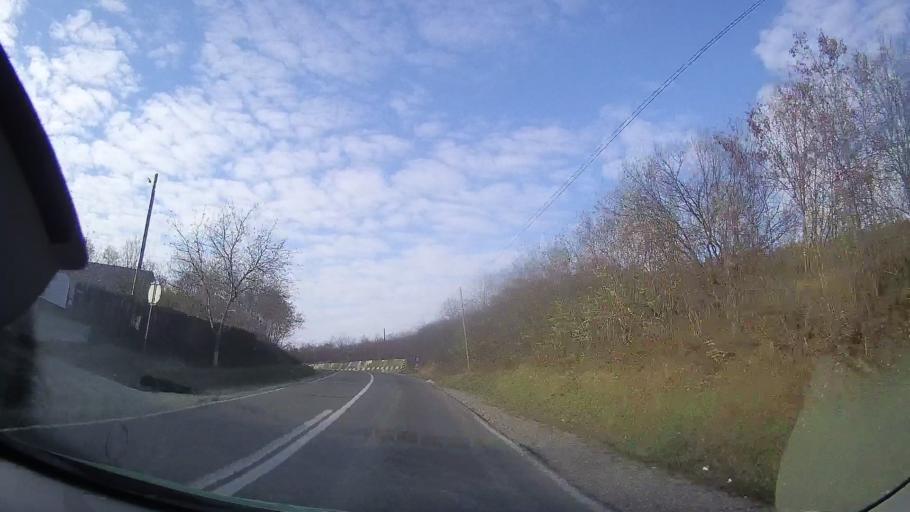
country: RO
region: Cluj
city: Jucu Herghelia
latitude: 46.8106
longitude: 23.8358
